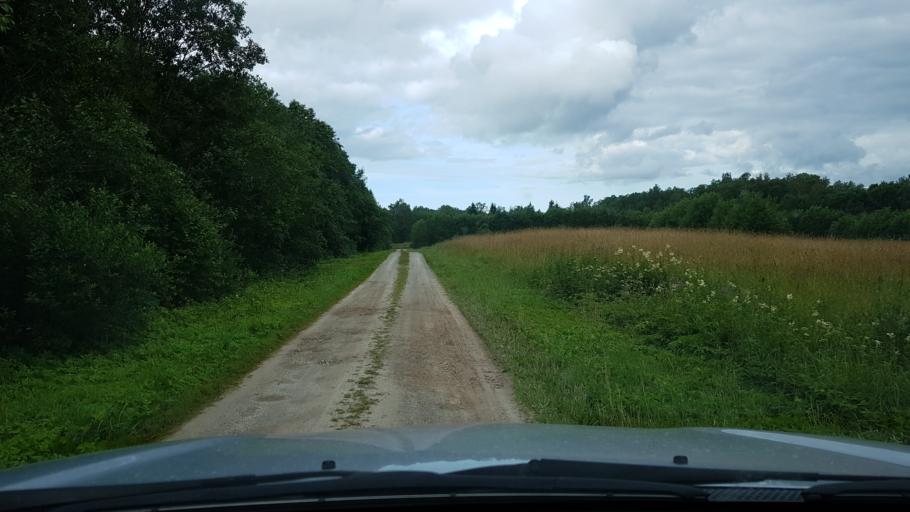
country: EE
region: Ida-Virumaa
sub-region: Narva-Joesuu linn
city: Narva-Joesuu
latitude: 59.4042
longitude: 27.9631
